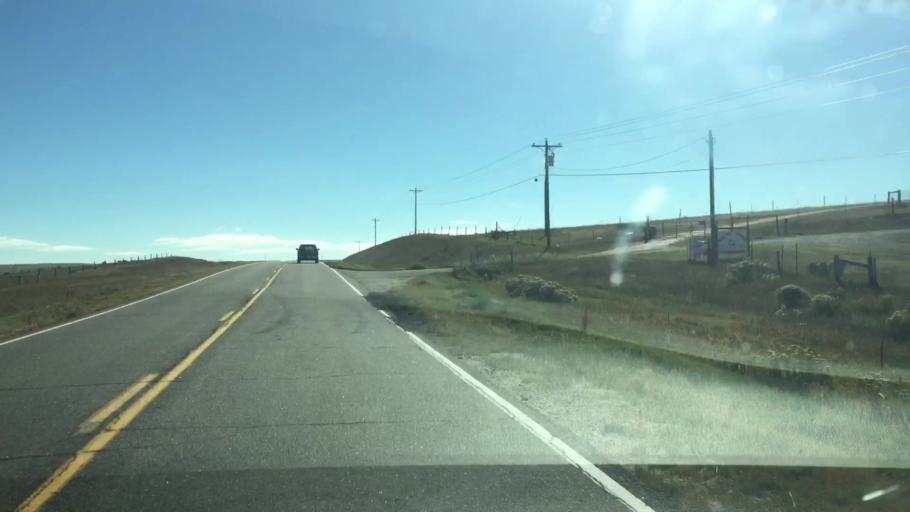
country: US
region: Colorado
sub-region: Elbert County
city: Kiowa
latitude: 39.3514
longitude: -104.4924
